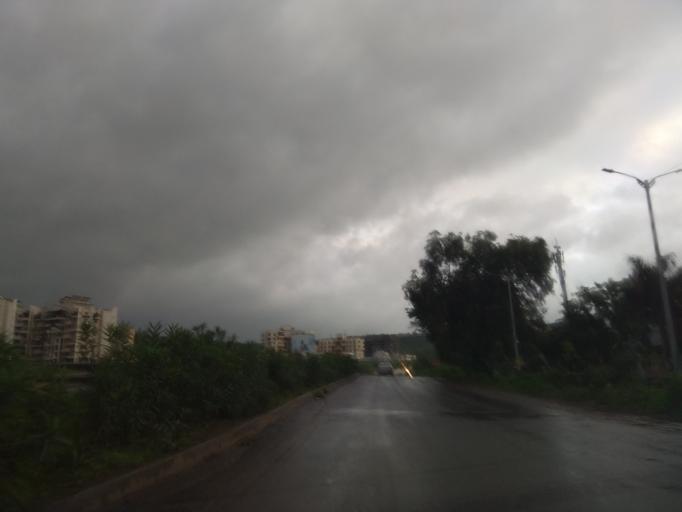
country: IN
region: Maharashtra
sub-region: Pune Division
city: Kharakvasla
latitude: 18.4903
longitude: 73.7916
